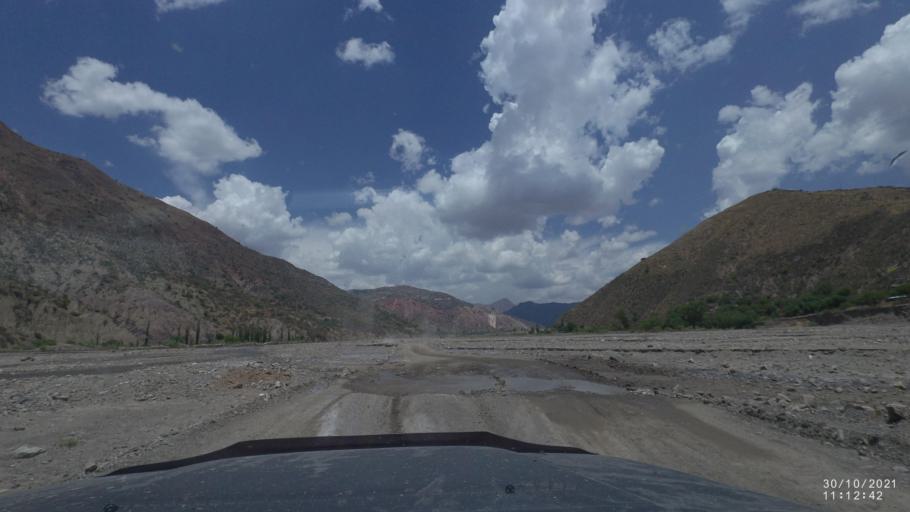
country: BO
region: Cochabamba
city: Sipe Sipe
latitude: -17.5258
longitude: -66.5718
